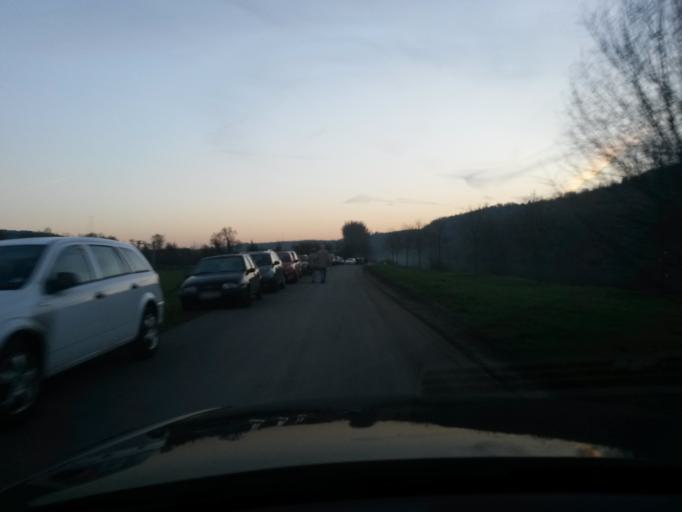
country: DE
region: Bavaria
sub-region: Regierungsbezirk Unterfranken
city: Sommerhausen
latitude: 49.7016
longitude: 10.0225
